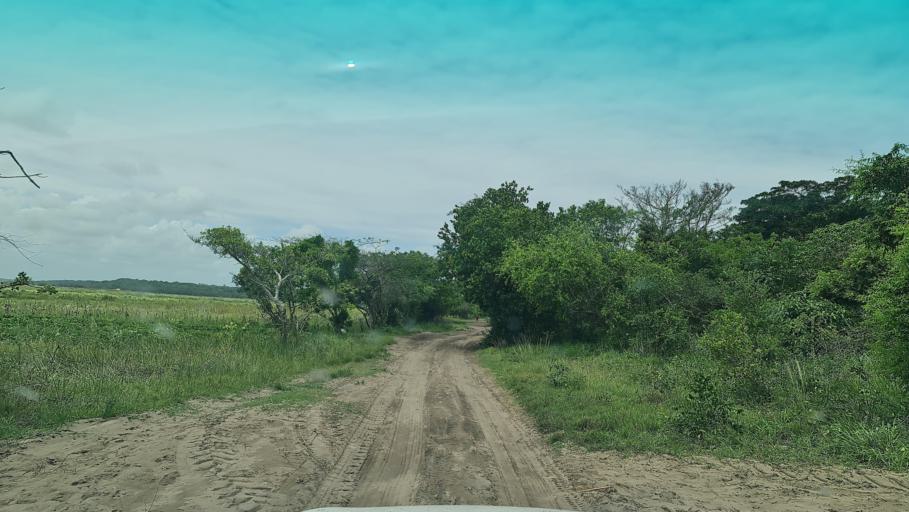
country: MZ
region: Maputo
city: Manhica
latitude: -25.5201
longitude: 32.8641
